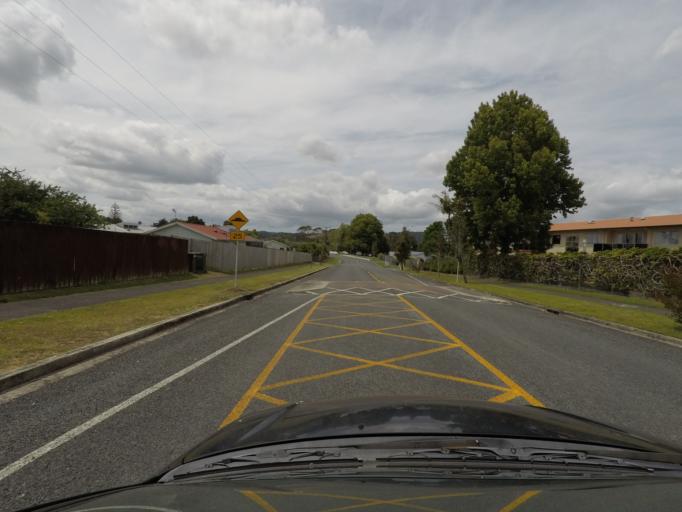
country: NZ
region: Northland
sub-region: Whangarei
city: Whangarei
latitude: -35.6862
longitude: 174.3342
